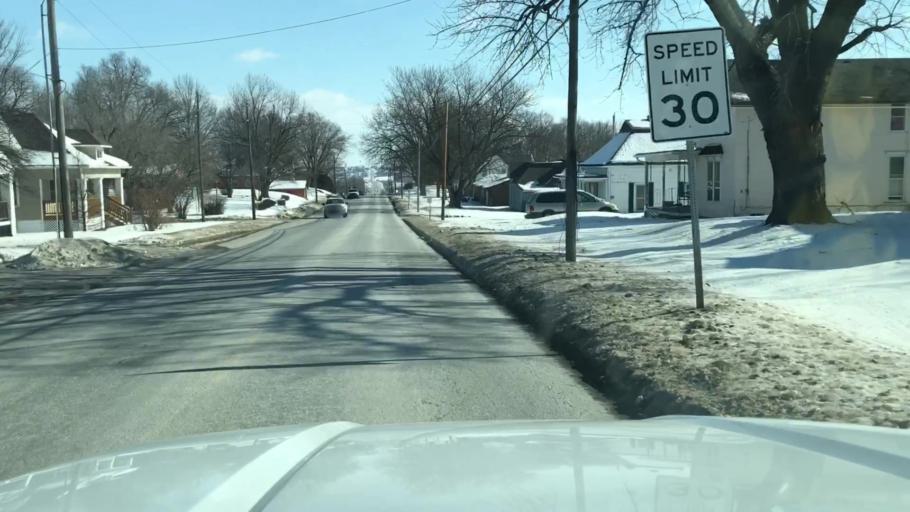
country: US
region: Missouri
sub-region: Nodaway County
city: Maryville
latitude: 40.3455
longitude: -94.8655
